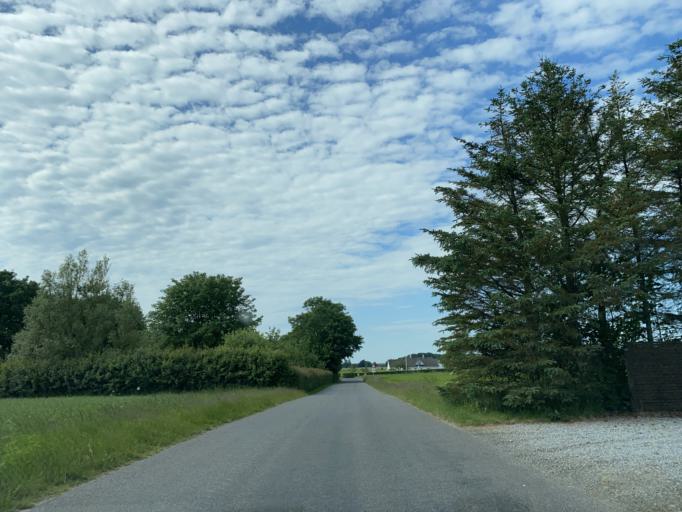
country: DK
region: Central Jutland
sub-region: Favrskov Kommune
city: Hammel
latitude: 56.2051
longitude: 9.8653
